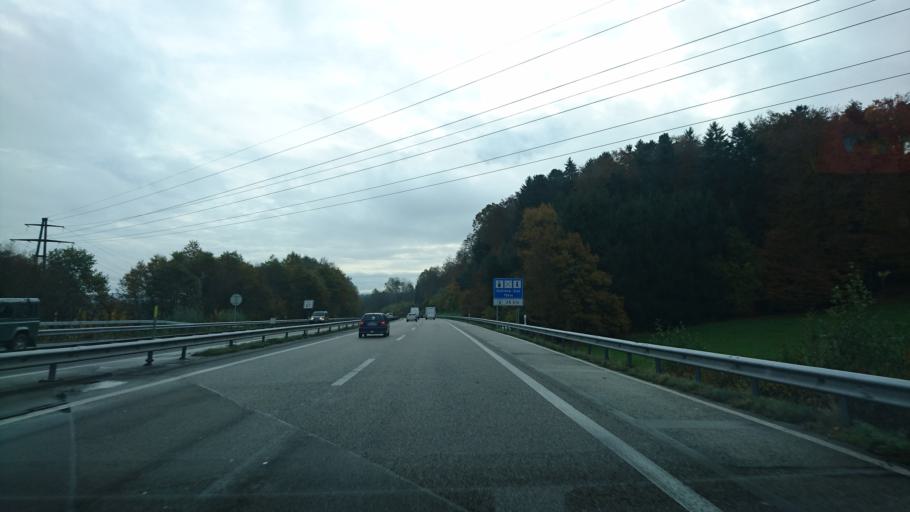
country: CH
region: Aargau
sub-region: Bezirk Zofingen
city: Kolliken
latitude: 47.3227
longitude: 8.0071
